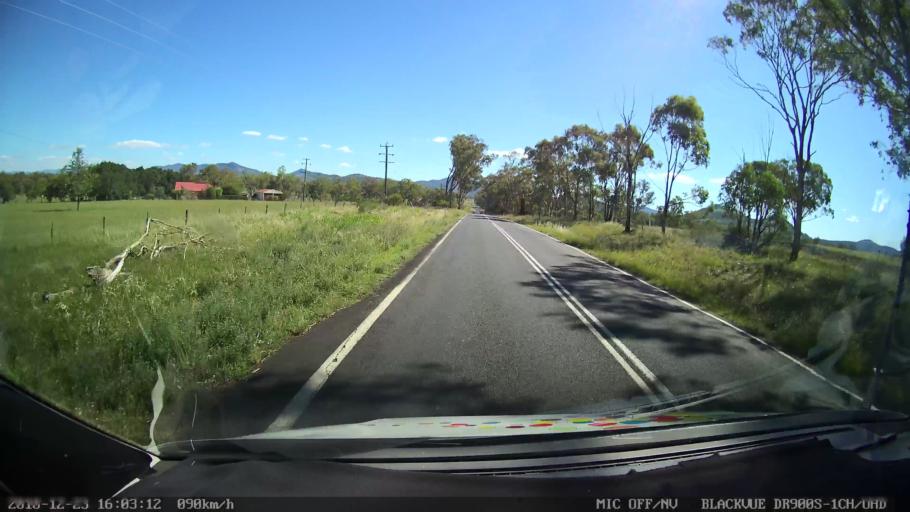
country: AU
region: New South Wales
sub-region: Tamworth Municipality
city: Phillip
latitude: -31.2408
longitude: 150.8027
